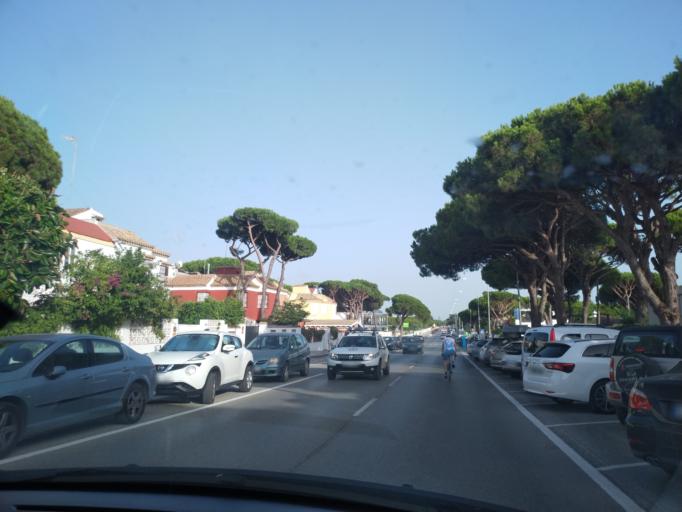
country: ES
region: Andalusia
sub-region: Provincia de Cadiz
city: Chiclana de la Frontera
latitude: 36.3755
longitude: -6.1857
